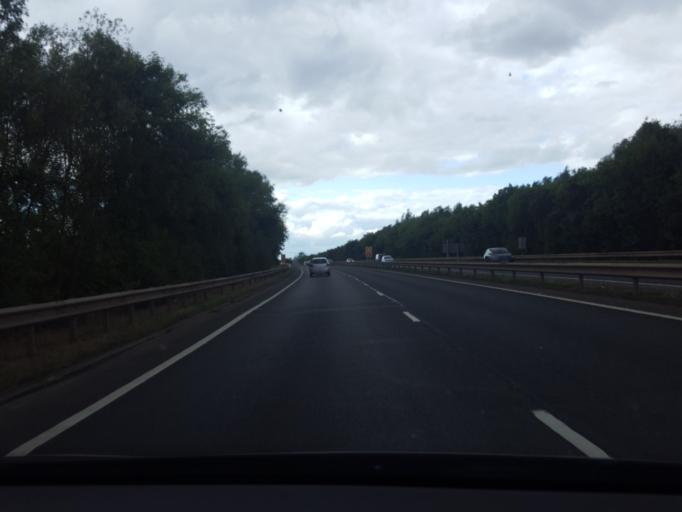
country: GB
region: England
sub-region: Leicestershire
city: Barrow upon Soar
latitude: 52.7367
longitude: -1.1385
